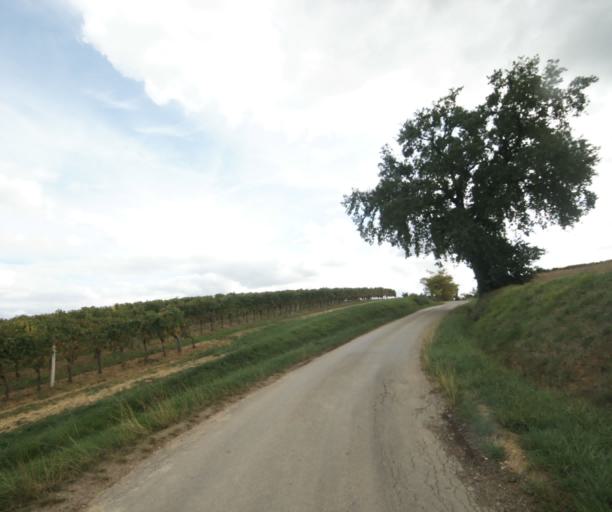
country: FR
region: Midi-Pyrenees
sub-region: Departement du Gers
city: Gondrin
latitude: 43.8687
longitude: 0.2501
